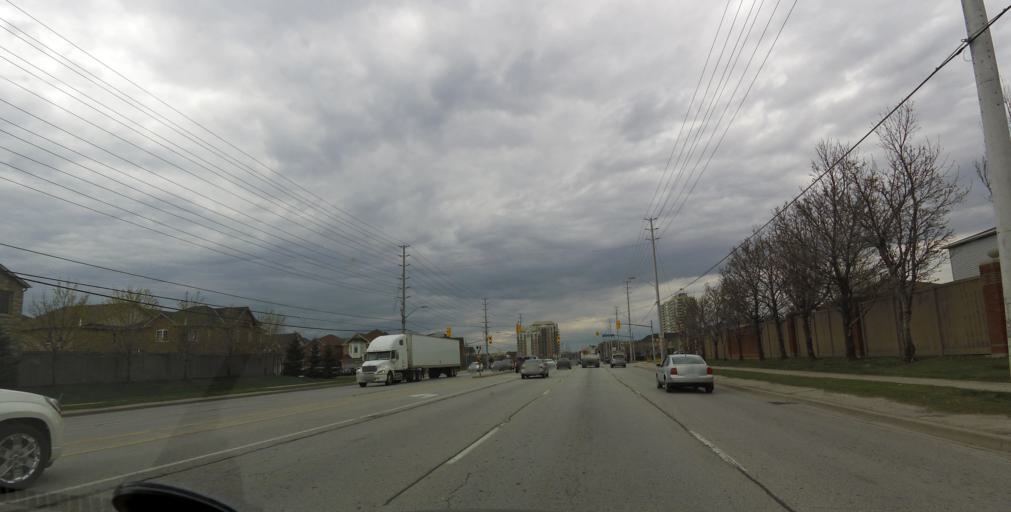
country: CA
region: Ontario
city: Mississauga
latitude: 43.5896
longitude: -79.6654
